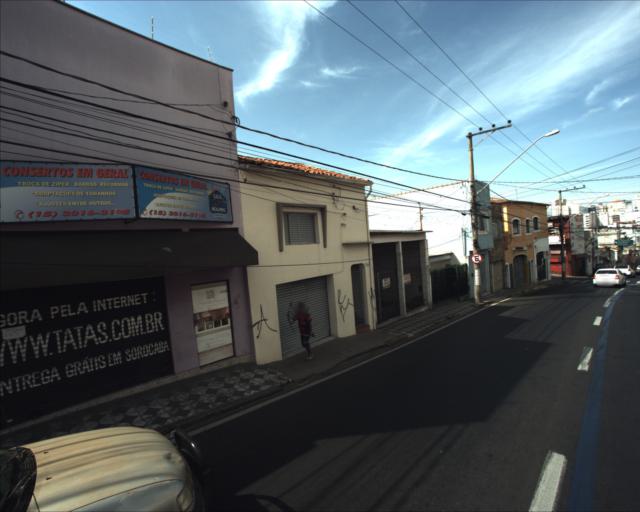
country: BR
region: Sao Paulo
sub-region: Sorocaba
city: Sorocaba
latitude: -23.4932
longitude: -47.4594
